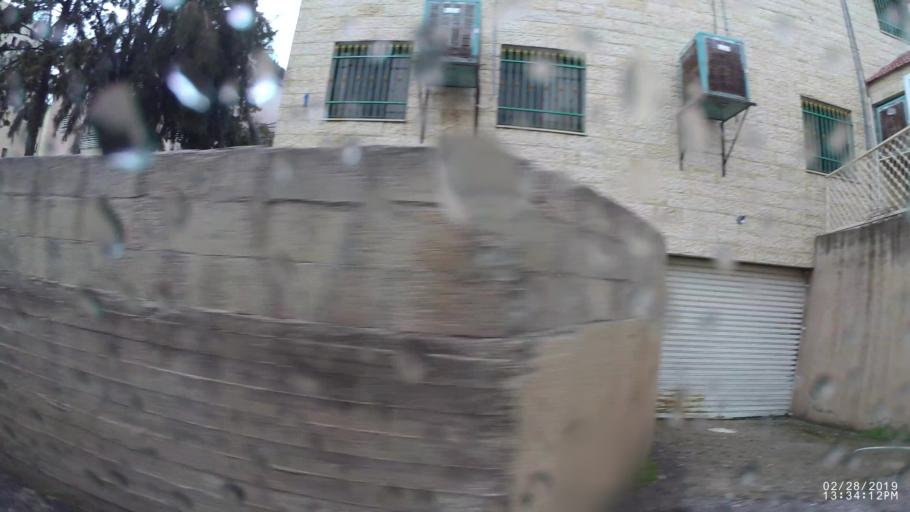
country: JO
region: Amman
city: Al Jubayhah
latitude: 32.0240
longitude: 35.8750
